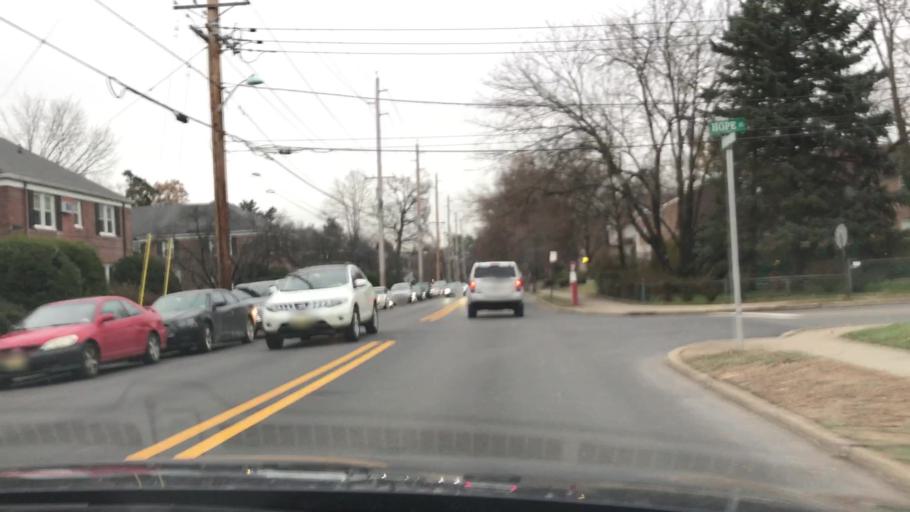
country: US
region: New Jersey
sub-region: Bergen County
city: Ridgewood
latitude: 40.9783
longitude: -74.1122
